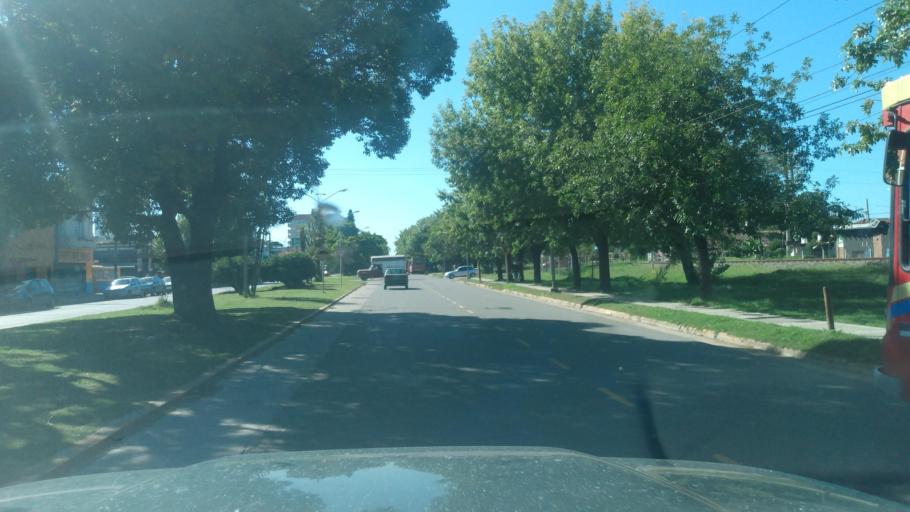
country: AR
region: Buenos Aires
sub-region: Partido de General Rodriguez
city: General Rodriguez
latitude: -34.6074
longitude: -58.9581
